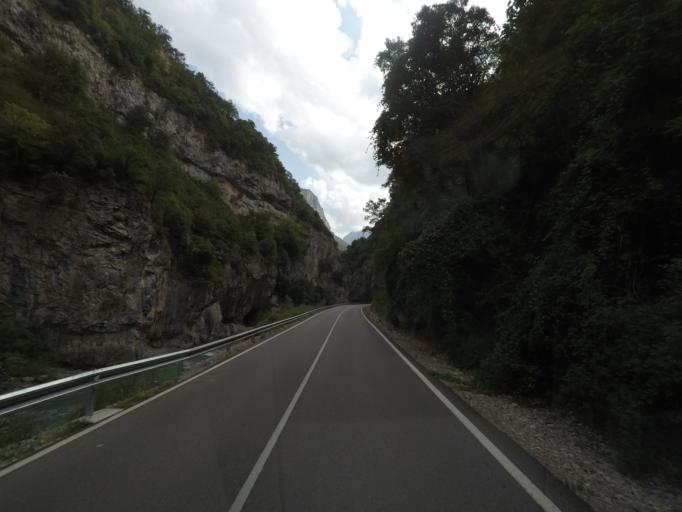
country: ES
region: Aragon
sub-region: Provincia de Huesca
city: Puertolas
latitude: 42.5603
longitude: 0.2045
